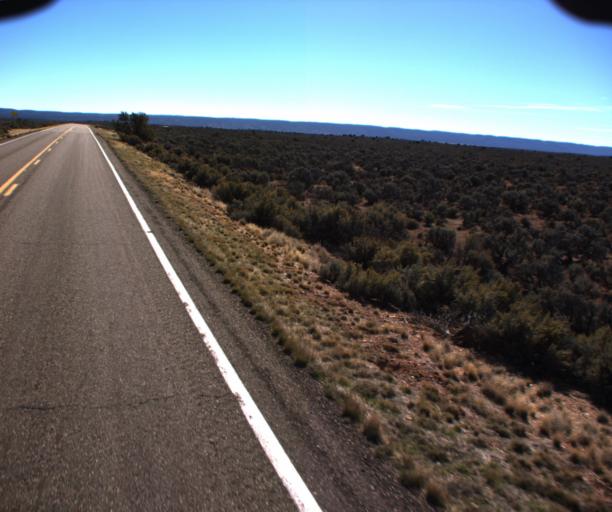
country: US
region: Arizona
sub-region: Coconino County
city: Fredonia
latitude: 36.8923
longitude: -112.3576
